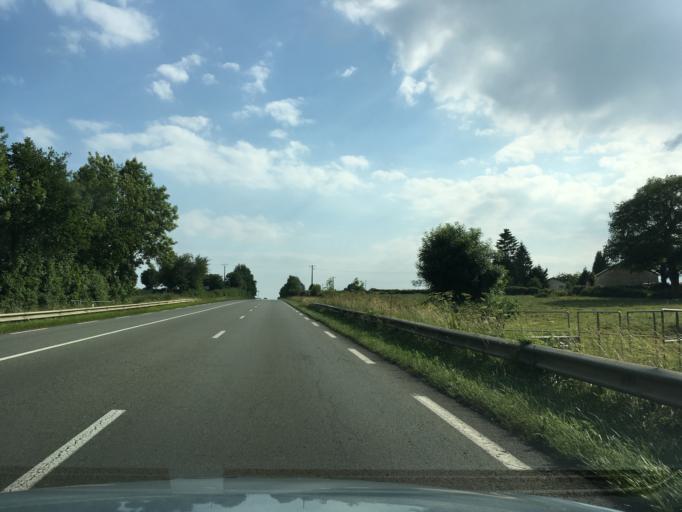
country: FR
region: Poitou-Charentes
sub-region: Departement des Deux-Sevres
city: Saint-Pardoux
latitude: 46.5561
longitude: -0.3070
